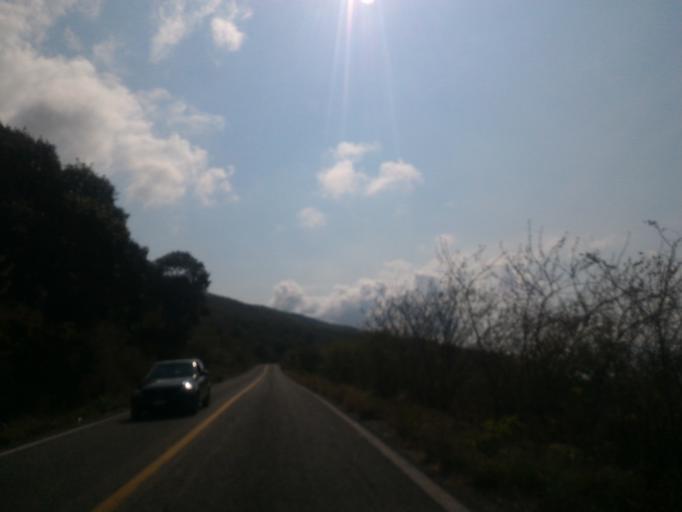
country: MX
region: Michoacan
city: Coahuayana Viejo
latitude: 18.4862
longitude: -103.5710
